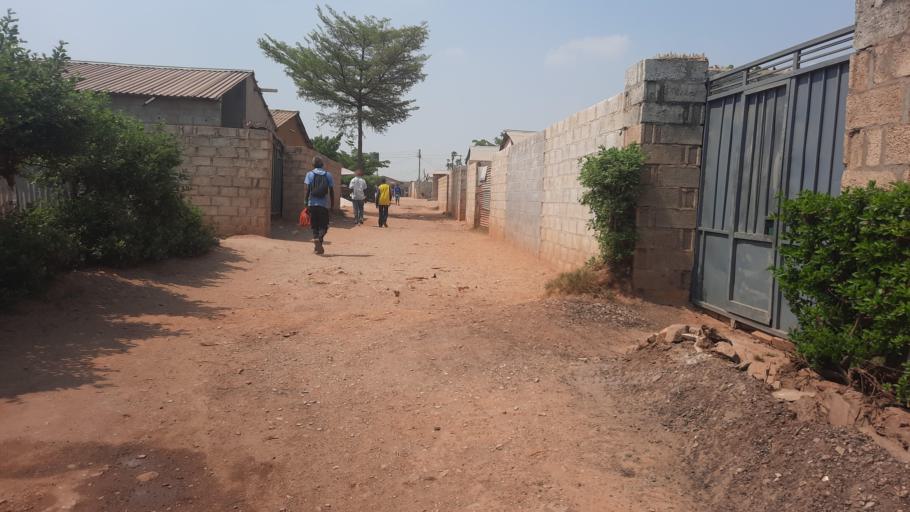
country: ZM
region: Lusaka
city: Lusaka
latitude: -15.4020
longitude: 28.3769
